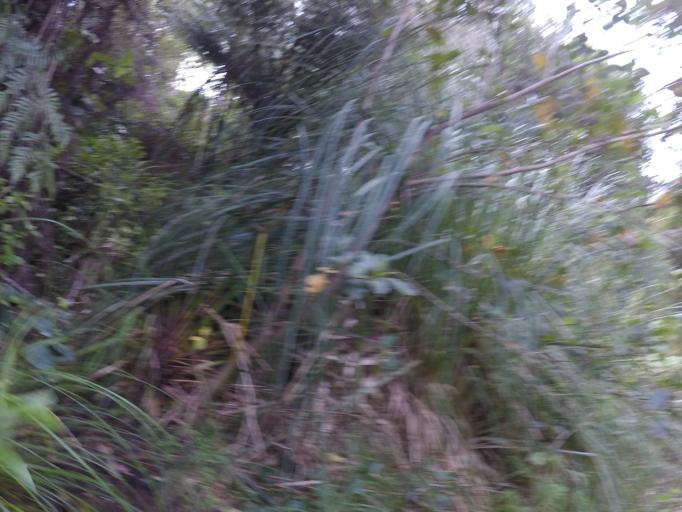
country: NZ
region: Bay of Plenty
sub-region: Western Bay of Plenty District
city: Waihi Beach
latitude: -37.3805
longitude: 175.9335
